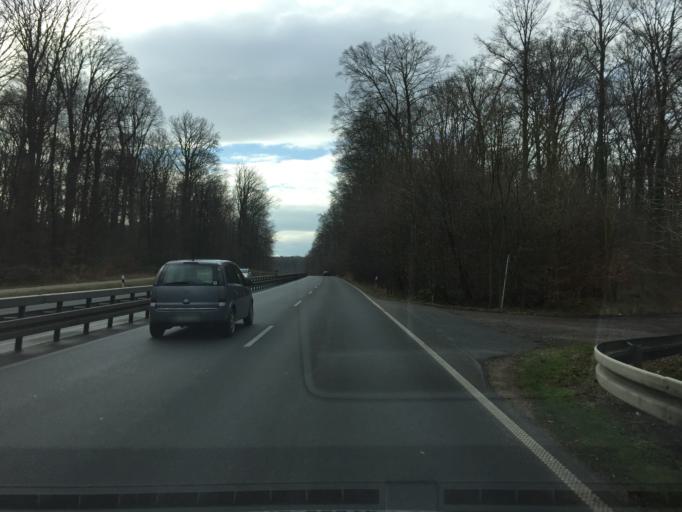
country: DE
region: Lower Saxony
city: Wennigsen
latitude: 52.2343
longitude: 9.6287
